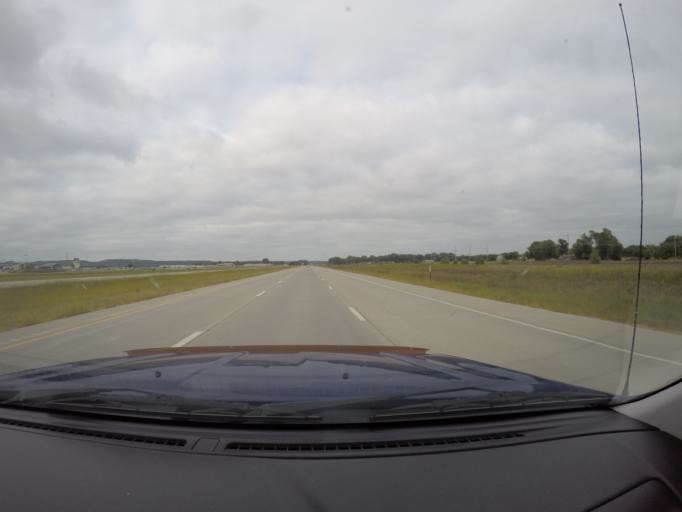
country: US
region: Kansas
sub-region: Riley County
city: Ogden
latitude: 39.1327
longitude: -96.6695
